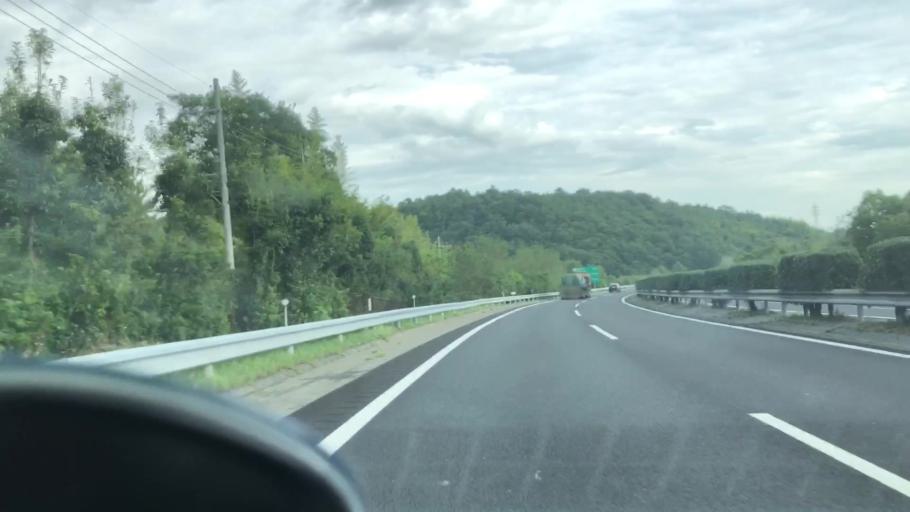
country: JP
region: Hyogo
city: Yashiro
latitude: 34.9397
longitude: 134.8768
